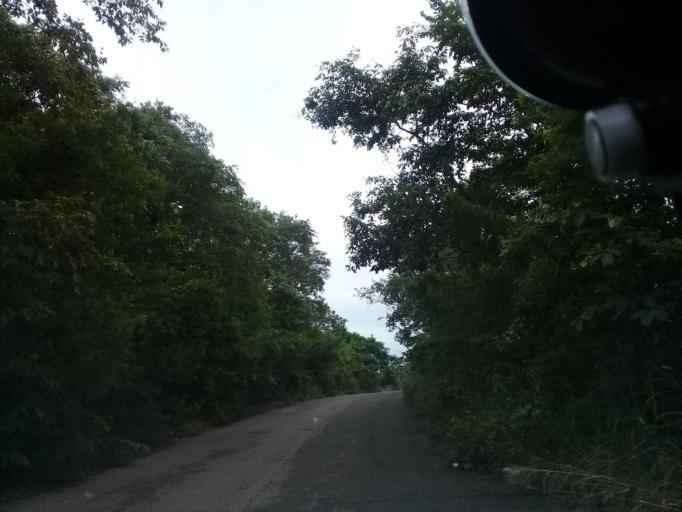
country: MX
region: Hidalgo
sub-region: Huejutla de Reyes
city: Chalahuiyapa
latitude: 21.2004
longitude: -98.3436
